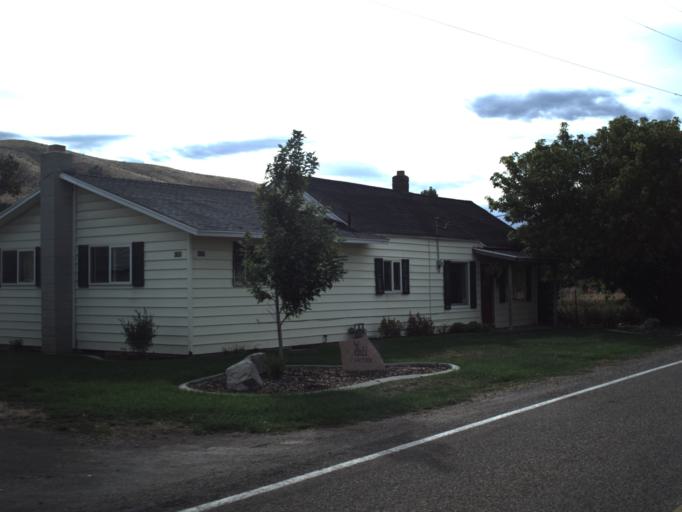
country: US
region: Utah
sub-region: Morgan County
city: Morgan
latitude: 40.9602
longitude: -111.6680
